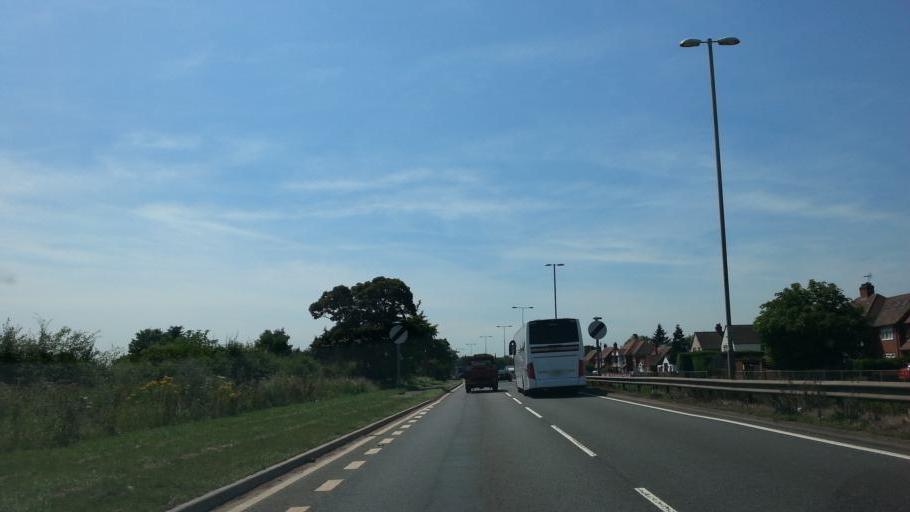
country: GB
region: England
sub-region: Staffordshire
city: Barton under Needwood
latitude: 52.7721
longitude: -1.6887
